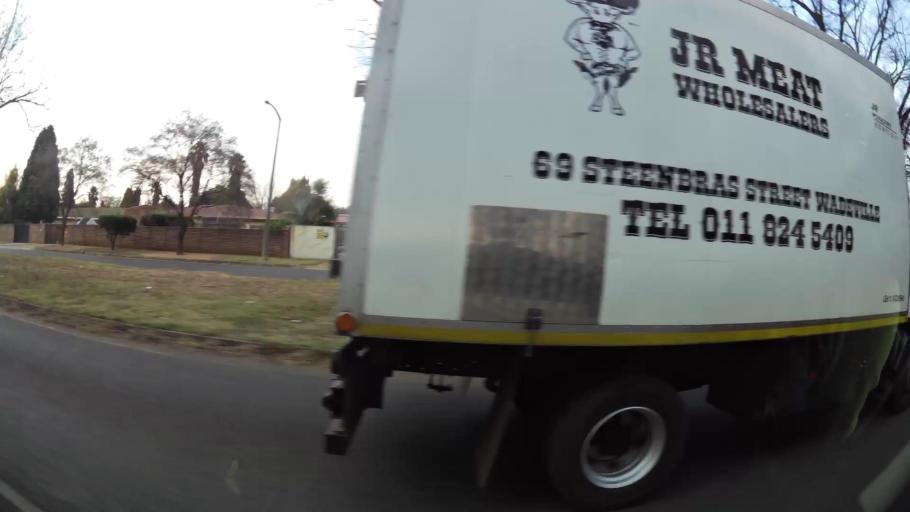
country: ZA
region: Gauteng
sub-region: Ekurhuleni Metropolitan Municipality
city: Benoni
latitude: -26.1509
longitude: 28.3008
